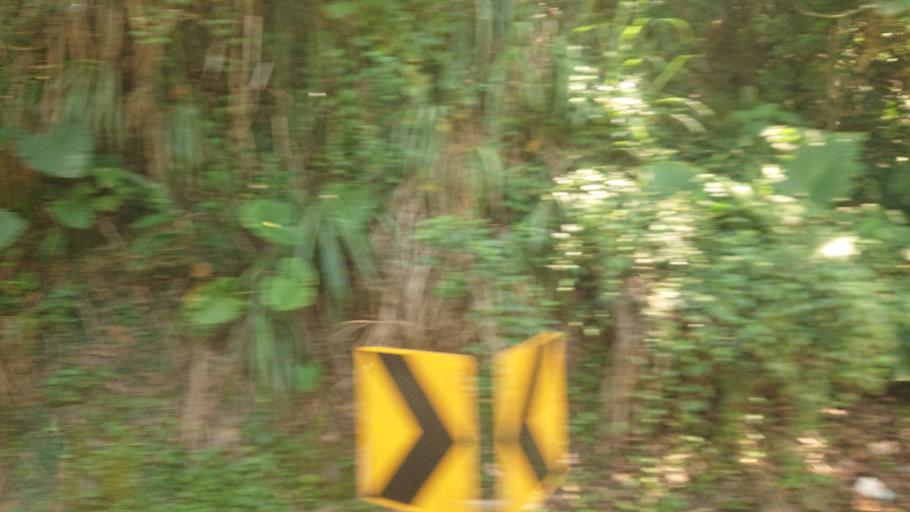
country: TW
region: Taiwan
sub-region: Nantou
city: Puli
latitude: 24.0496
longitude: 120.9358
